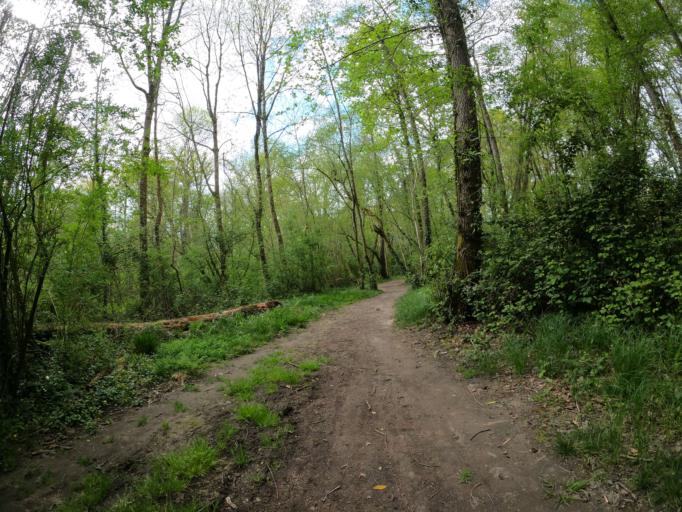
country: FR
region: Aquitaine
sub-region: Departement des Pyrenees-Atlantiques
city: Lons
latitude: 43.3225
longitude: -0.3918
